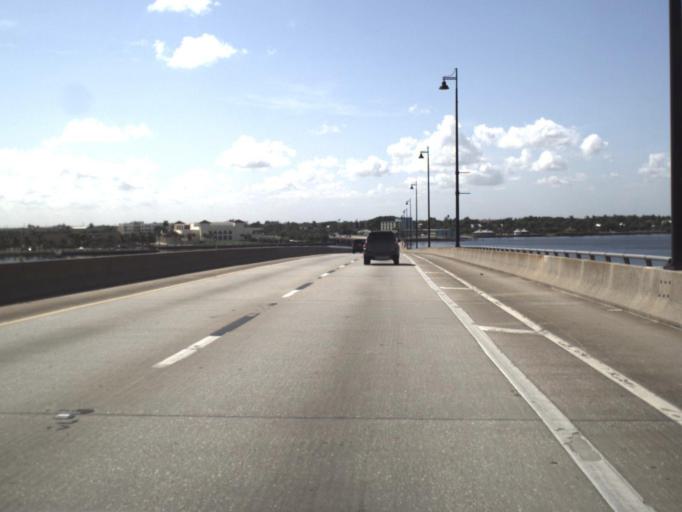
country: US
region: Florida
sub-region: Charlotte County
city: Charlotte Harbor
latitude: 26.9432
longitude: -82.0580
